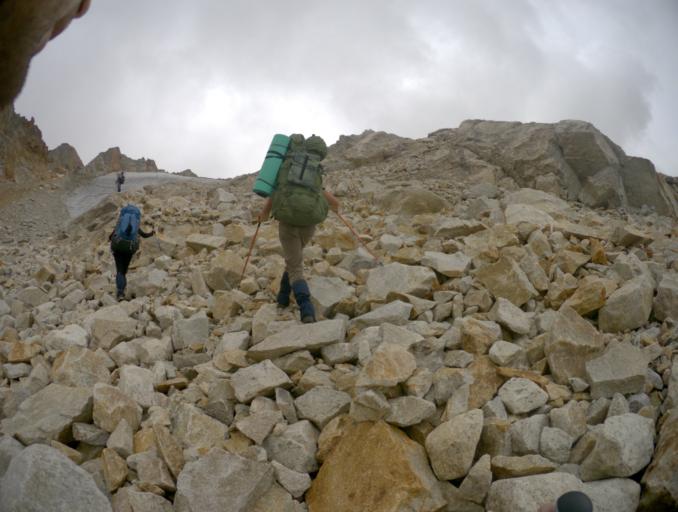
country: RU
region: Karachayevo-Cherkesiya
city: Uchkulan
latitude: 43.2798
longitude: 42.1120
